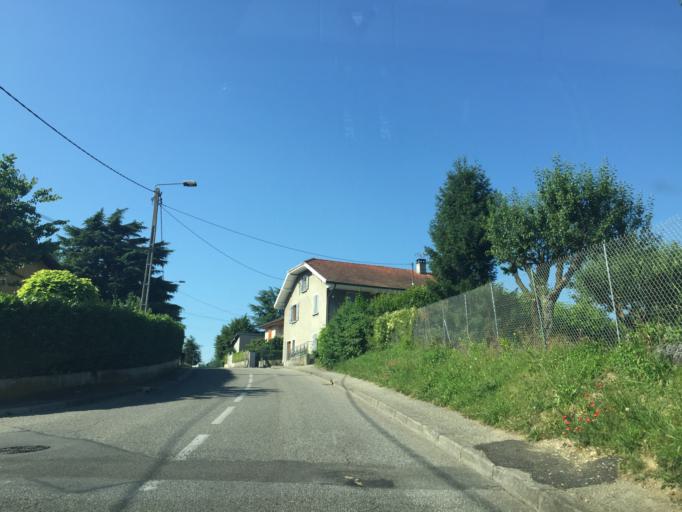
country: FR
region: Rhone-Alpes
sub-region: Departement de la Savoie
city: Drumettaz-Clarafond
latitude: 45.6665
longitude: 5.9108
